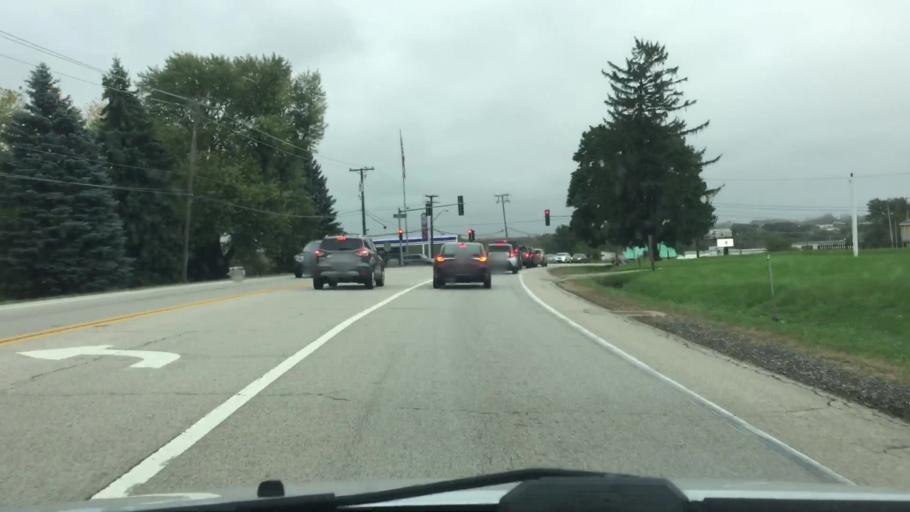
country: US
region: Illinois
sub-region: McHenry County
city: McCullom Lake
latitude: 42.3796
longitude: -88.2703
